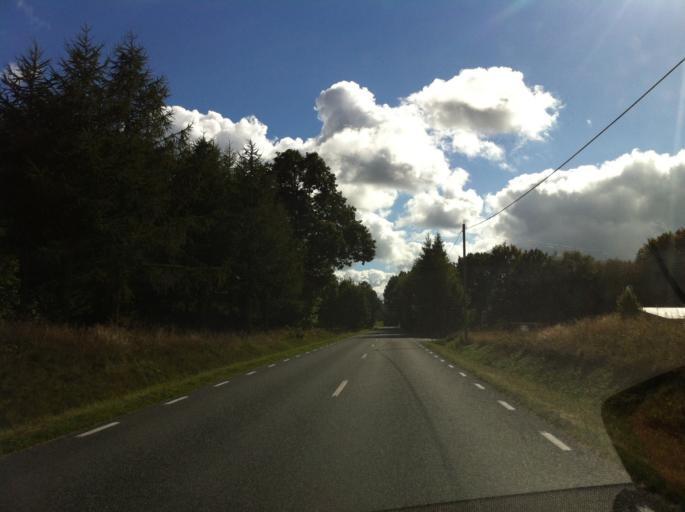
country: SE
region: Skane
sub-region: Kristianstads Kommun
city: Degeberga
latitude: 55.7785
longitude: 13.8888
